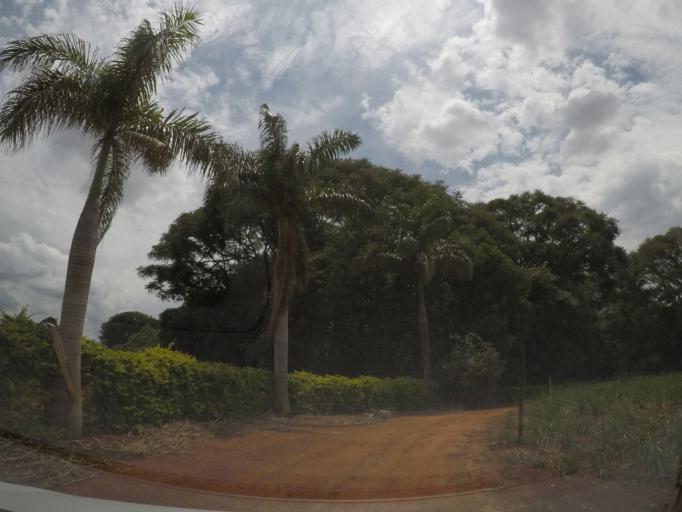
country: BR
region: Sao Paulo
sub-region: Sumare
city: Sumare
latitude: -22.8535
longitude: -47.3020
